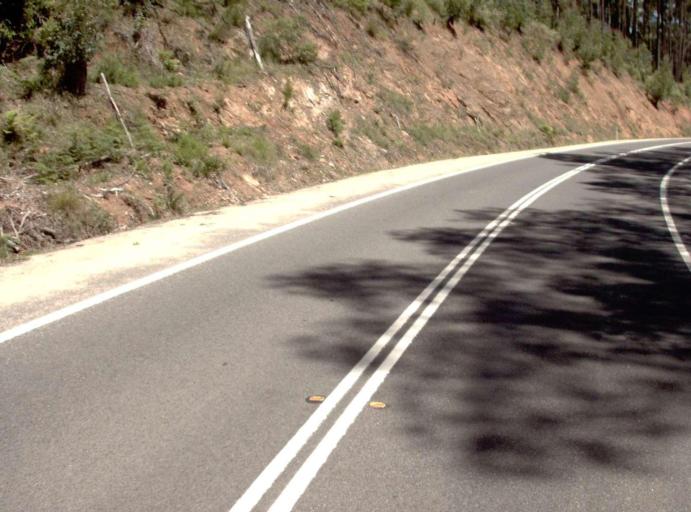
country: AU
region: New South Wales
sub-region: Bombala
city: Bombala
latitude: -37.5915
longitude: 148.9897
